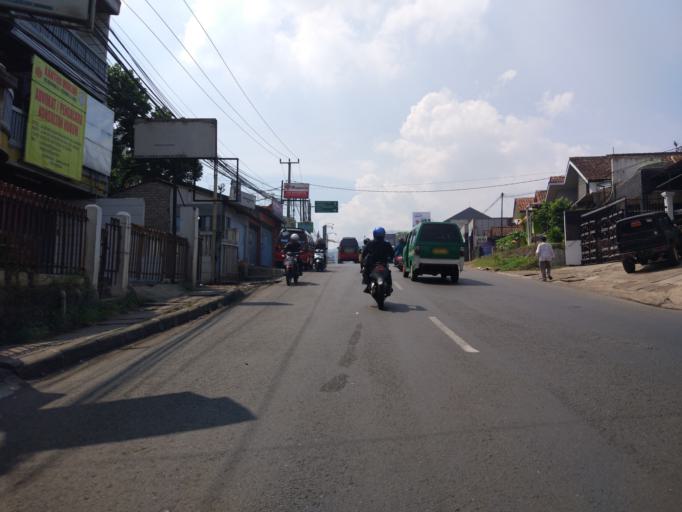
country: ID
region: West Java
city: Cileunyi
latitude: -6.9381
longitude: 107.7553
